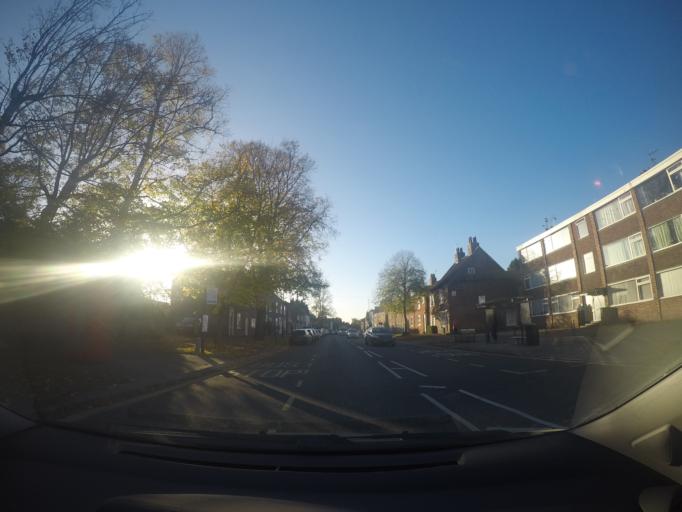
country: GB
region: England
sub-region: City of York
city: Fulford
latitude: 53.9360
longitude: -1.0721
